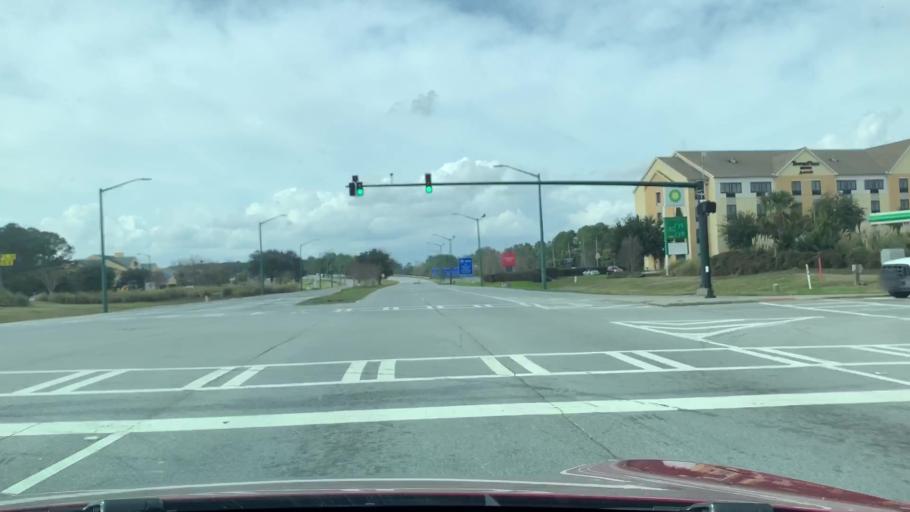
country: US
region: Georgia
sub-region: Chatham County
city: Pooler
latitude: 32.1391
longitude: -81.2335
